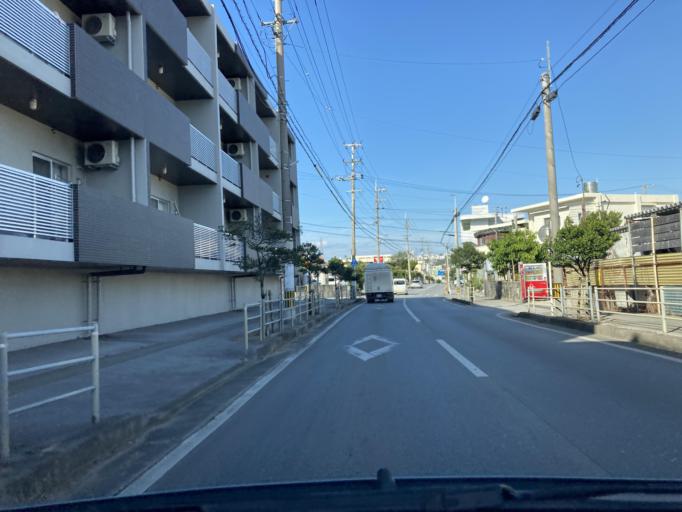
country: JP
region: Okinawa
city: Tomigusuku
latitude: 26.1824
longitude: 127.7068
